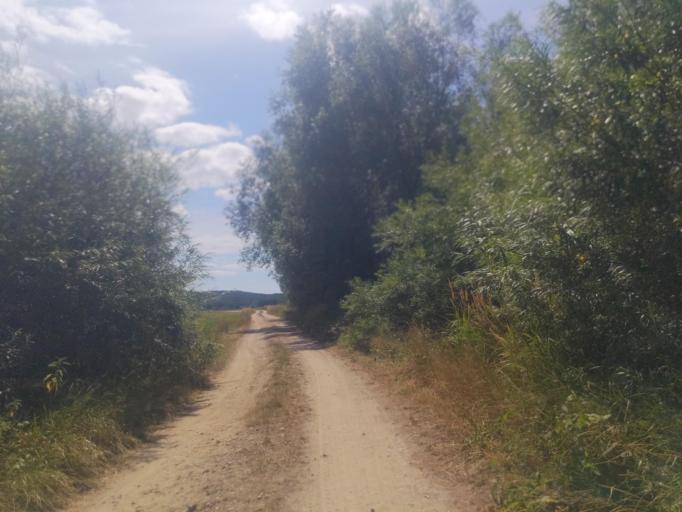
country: DE
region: Lower Saxony
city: Neu Darchau
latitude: 53.2519
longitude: 10.8470
